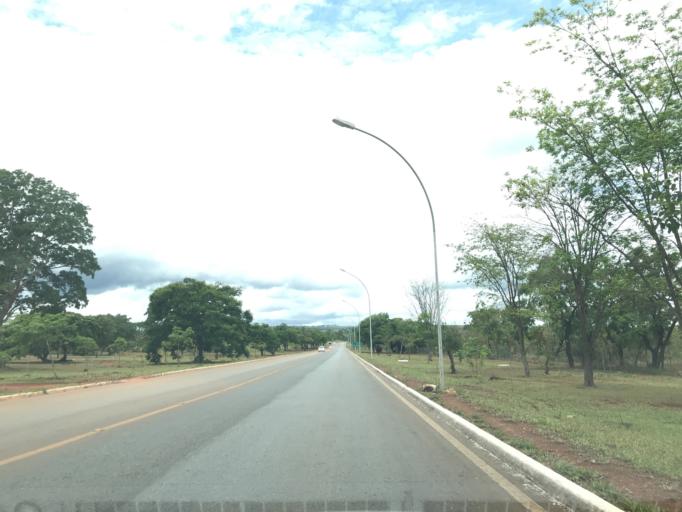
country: BR
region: Federal District
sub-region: Brasilia
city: Brasilia
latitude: -15.7969
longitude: -47.8408
